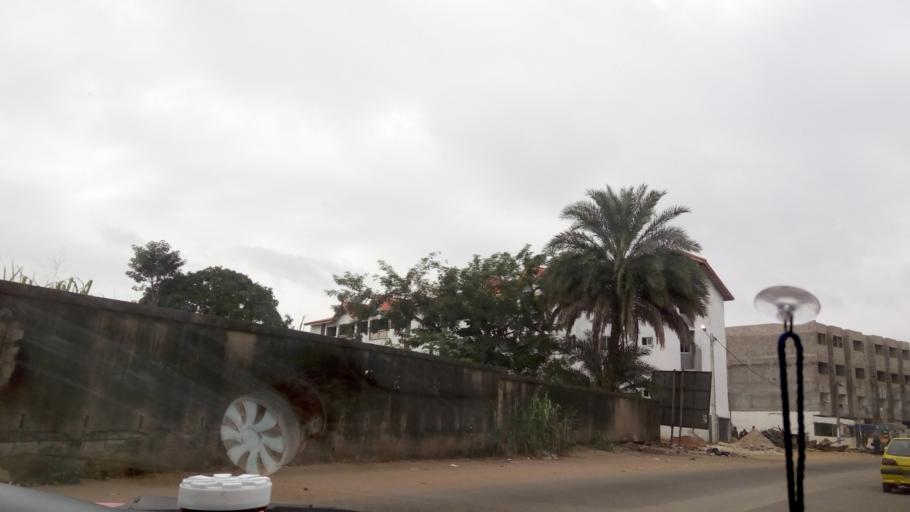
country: CI
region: Lagunes
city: Abidjan
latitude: 5.3430
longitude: -3.9742
